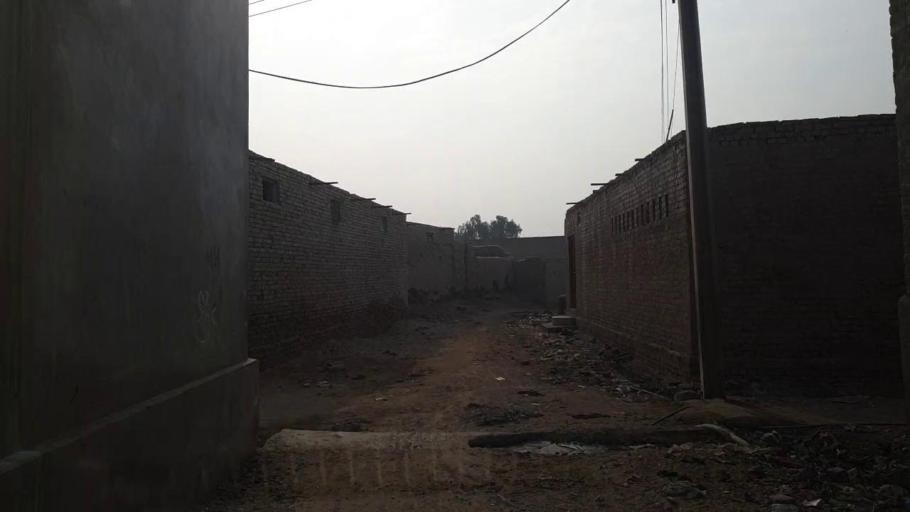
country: PK
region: Sindh
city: Sann
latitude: 26.1092
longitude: 68.0834
